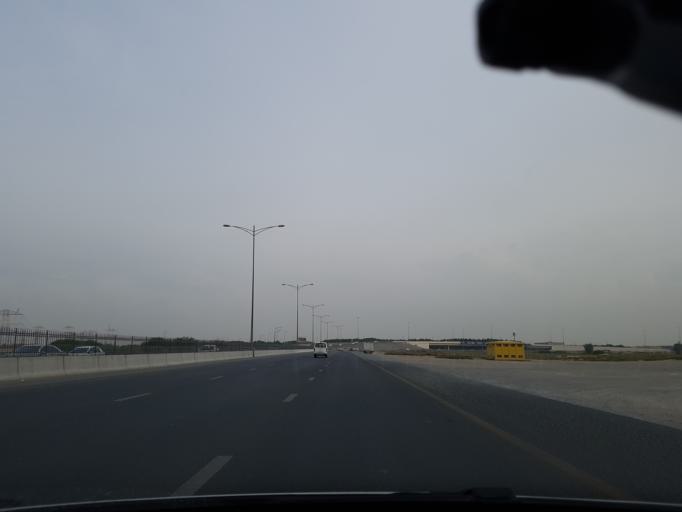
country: AE
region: Ajman
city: Ajman
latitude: 25.3614
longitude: 55.4772
